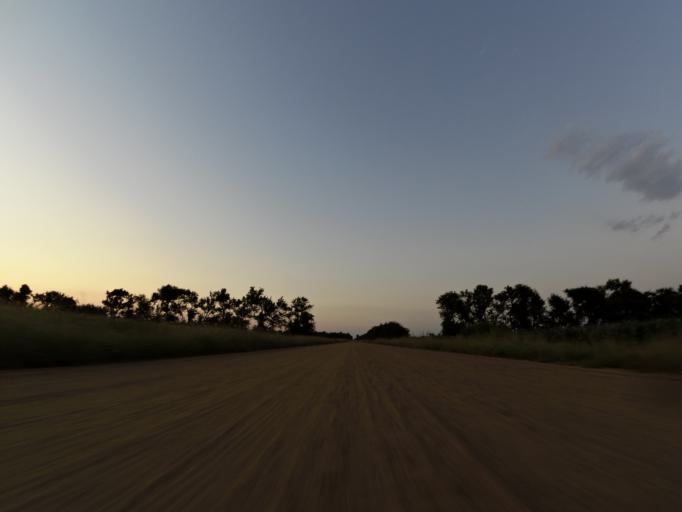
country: US
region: Kansas
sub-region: Reno County
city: South Hutchinson
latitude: 37.9619
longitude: -98.0319
